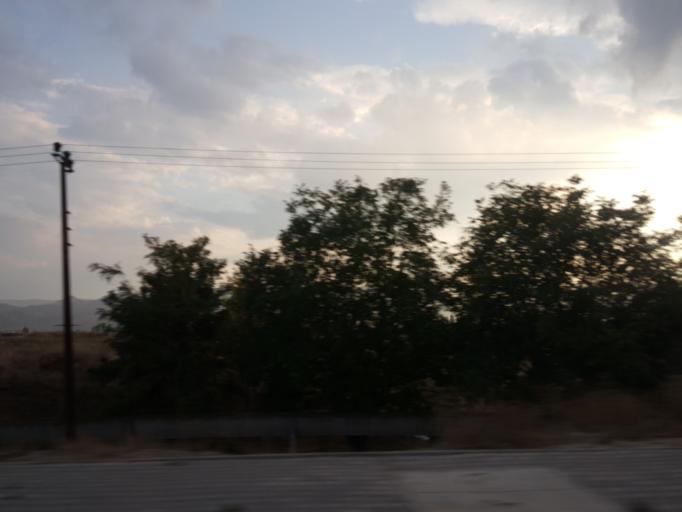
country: TR
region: Amasya
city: Gumushacikoy
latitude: 40.8755
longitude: 35.2358
